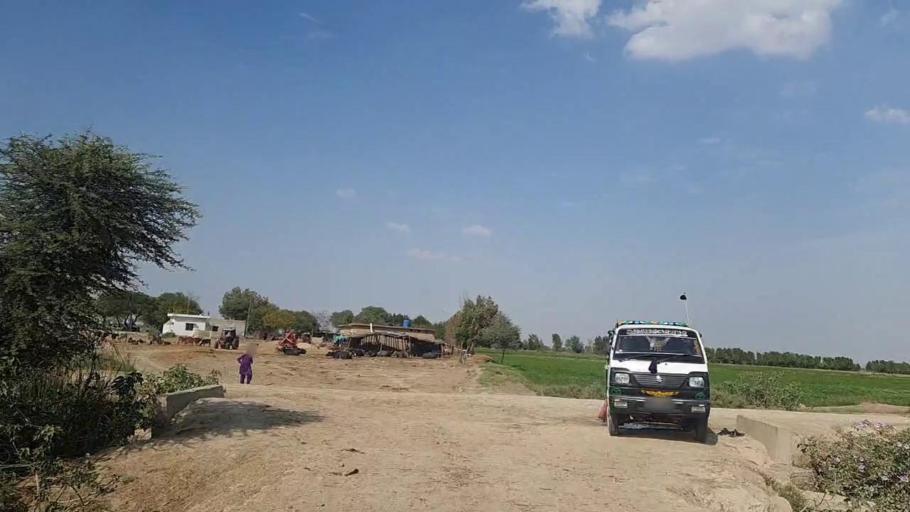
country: PK
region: Sindh
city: Jati
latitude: 24.5214
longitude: 68.2943
